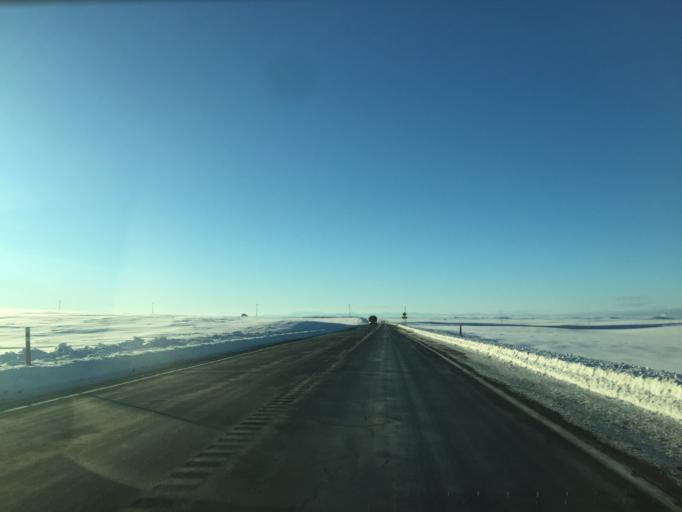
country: US
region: Washington
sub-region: Grant County
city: Soap Lake
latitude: 47.6199
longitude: -119.4213
